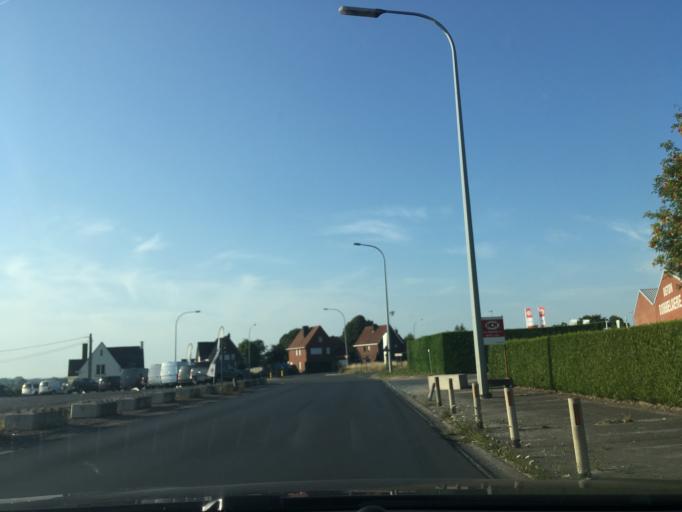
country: BE
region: Flanders
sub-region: Provincie West-Vlaanderen
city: Tielt
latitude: 51.0044
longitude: 3.3444
